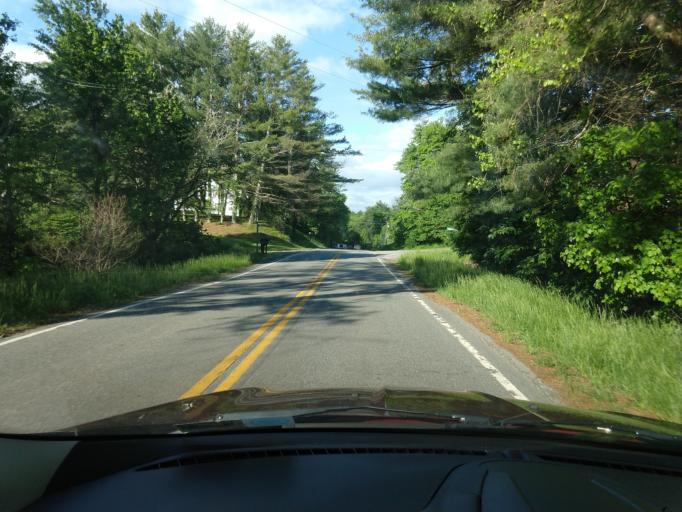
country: US
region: Virginia
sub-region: City of Galax
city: Galax
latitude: 36.7504
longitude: -80.9847
